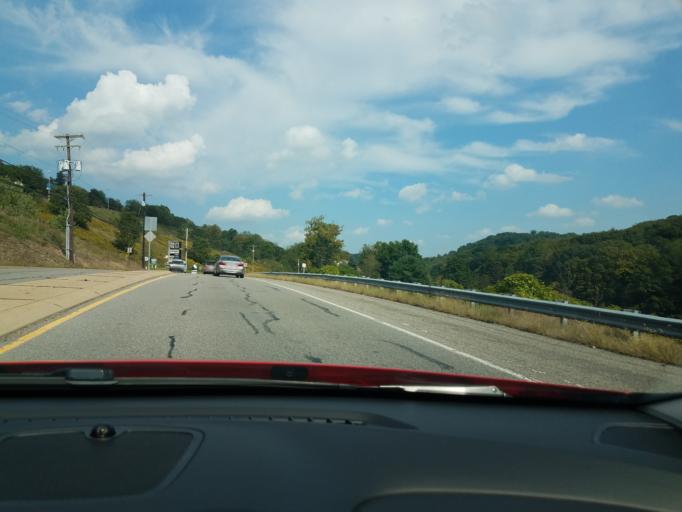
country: US
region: Pennsylvania
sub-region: Allegheny County
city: Ben Avon
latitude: 40.5314
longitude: -80.0687
